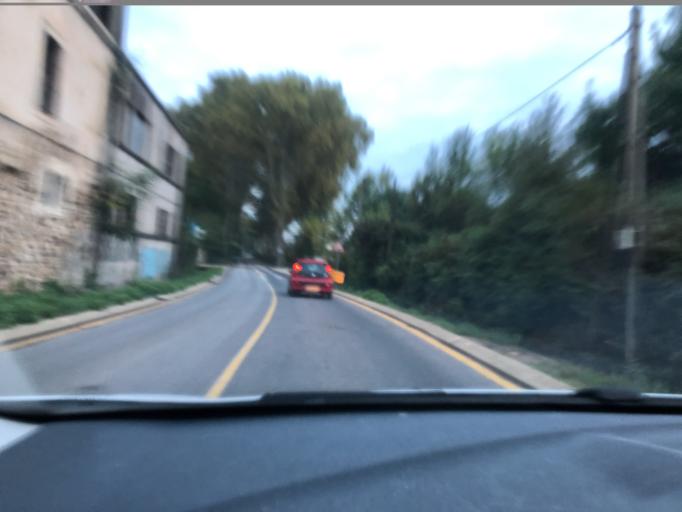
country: FR
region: Languedoc-Roussillon
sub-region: Departement de l'Herault
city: Montferrier-sur-Lez
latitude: 43.6630
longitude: 3.8630
